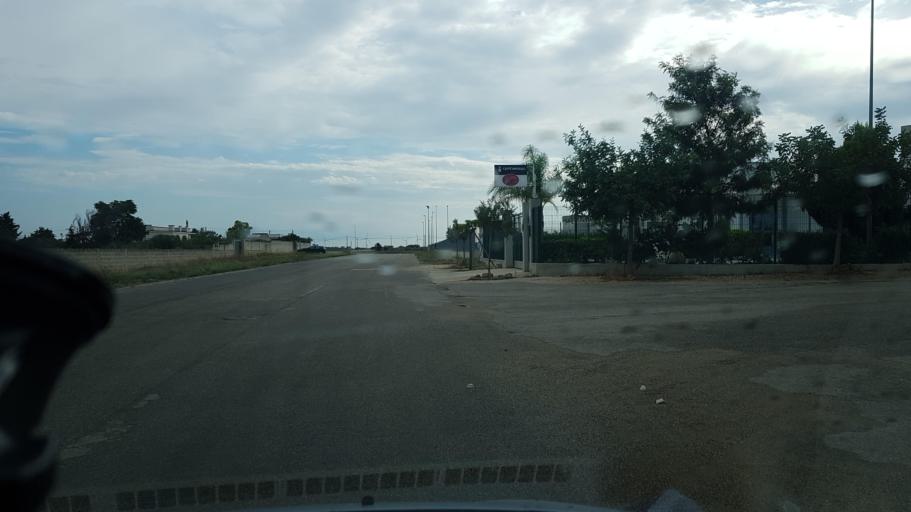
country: IT
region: Apulia
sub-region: Provincia di Brindisi
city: Torre Santa Susanna
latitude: 40.4702
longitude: 17.7243
